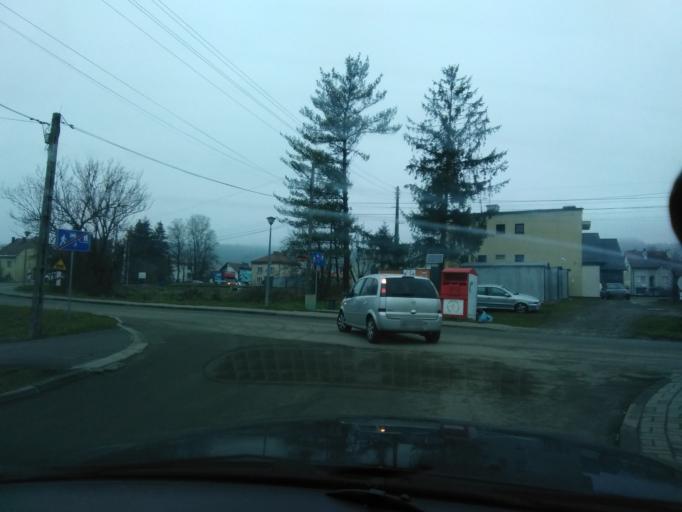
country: PL
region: Subcarpathian Voivodeship
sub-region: Powiat strzyzowski
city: Strzyzow
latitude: 49.8689
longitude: 21.7977
